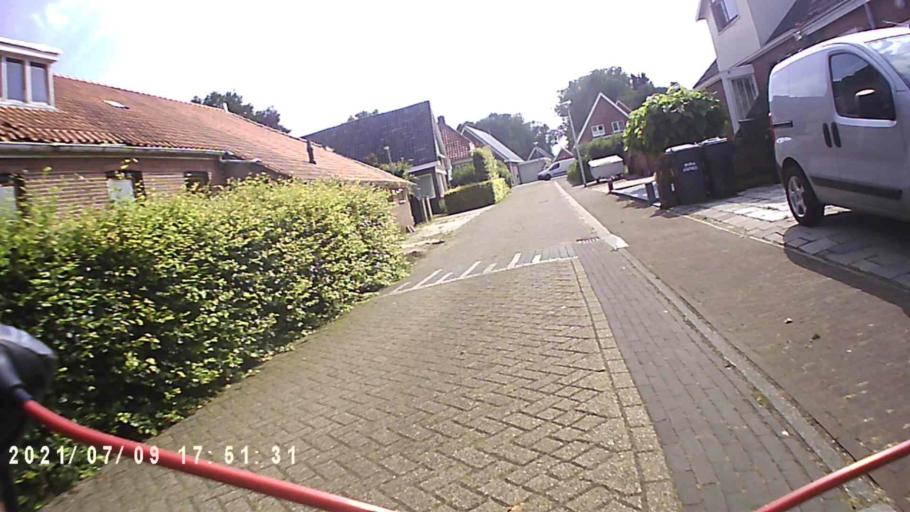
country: NL
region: Groningen
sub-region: Gemeente Vlagtwedde
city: Vlagtwedde
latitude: 53.0684
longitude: 7.0764
